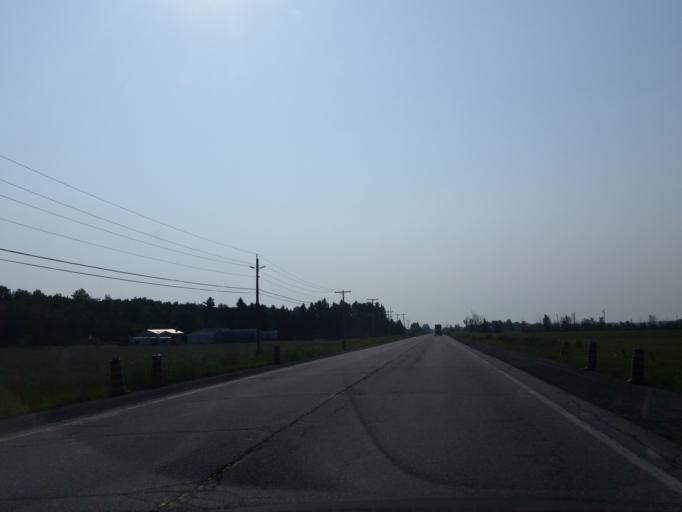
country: CA
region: Ontario
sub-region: Nipissing District
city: North Bay
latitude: 46.4180
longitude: -80.1506
